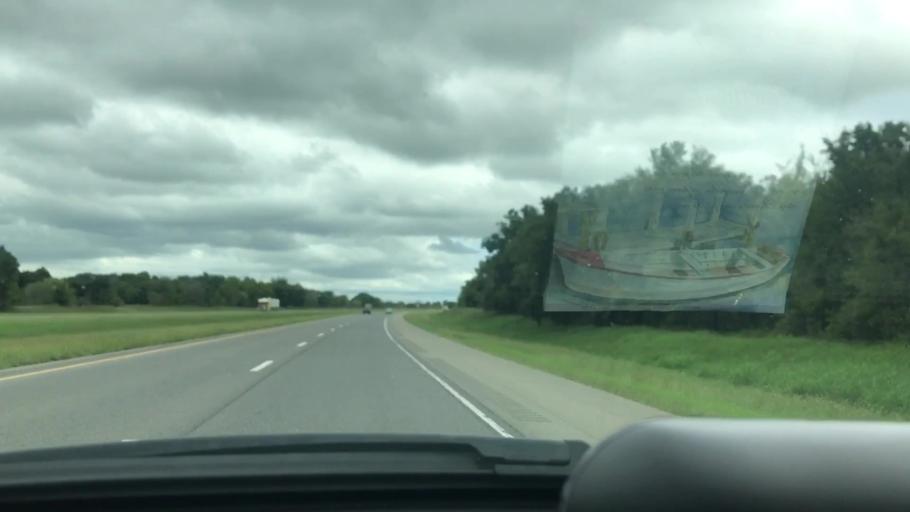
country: US
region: Oklahoma
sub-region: McIntosh County
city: Checotah
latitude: 35.5846
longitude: -95.4899
